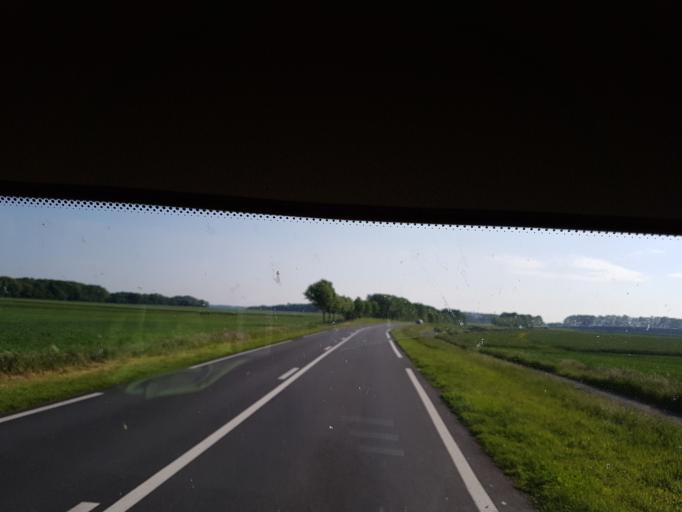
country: FR
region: Picardie
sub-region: Departement de la Somme
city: Crecy-en-Ponthieu
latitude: 50.1988
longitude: 1.8900
